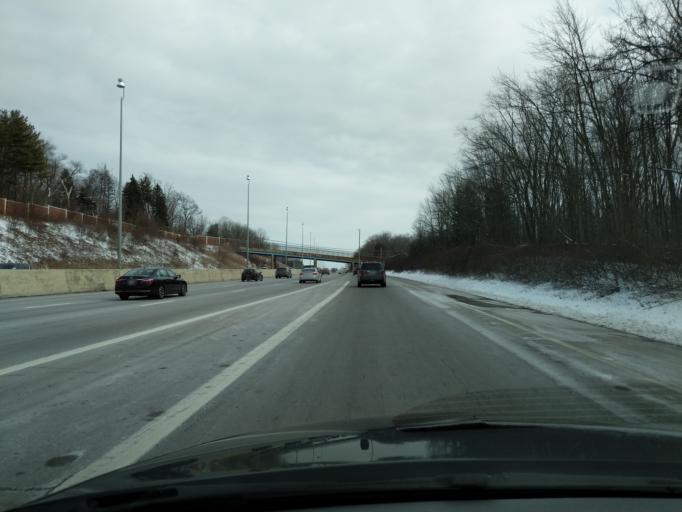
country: US
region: Ohio
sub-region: Summit County
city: Fairlawn
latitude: 41.1102
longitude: -81.6069
